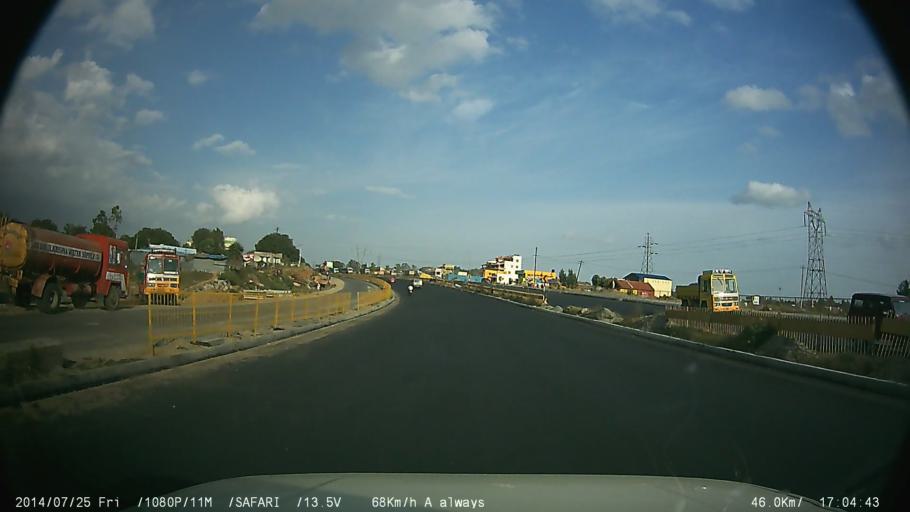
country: IN
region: Tamil Nadu
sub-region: Krishnagiri
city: Hosur
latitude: 12.7129
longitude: 77.8870
